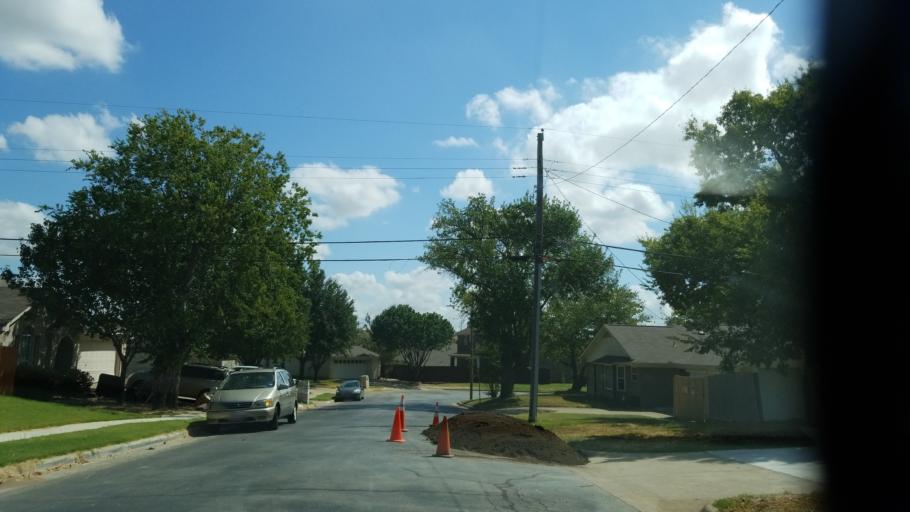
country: US
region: Texas
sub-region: Tarrant County
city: Euless
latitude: 32.8352
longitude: -97.0743
